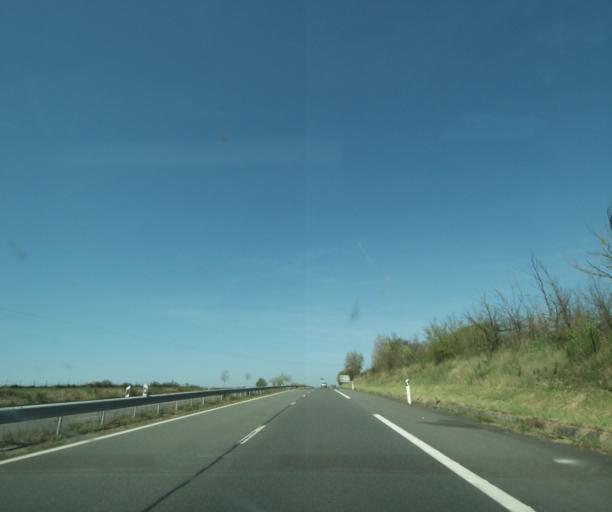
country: FR
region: Bourgogne
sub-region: Departement de la Nievre
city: Chaulgnes
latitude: 47.1284
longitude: 3.0479
